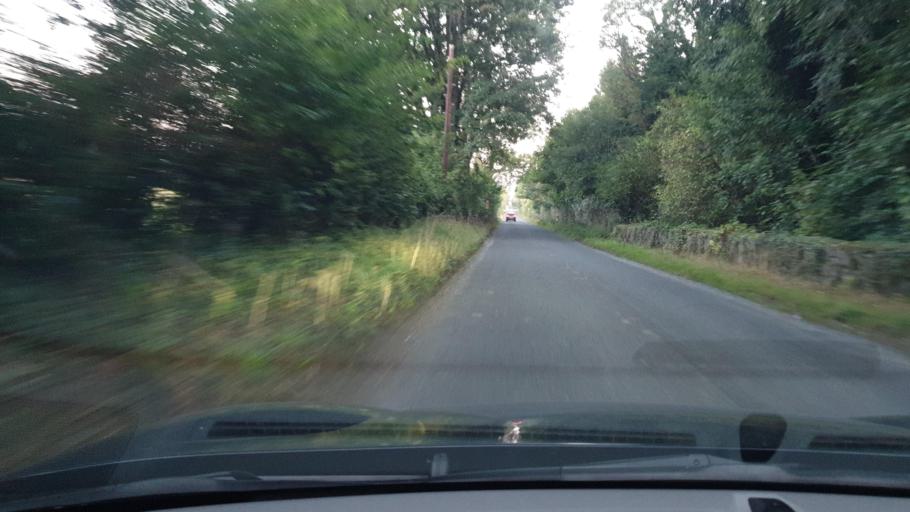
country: IE
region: Leinster
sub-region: Kildare
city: Prosperous
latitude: 53.3491
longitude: -6.7503
